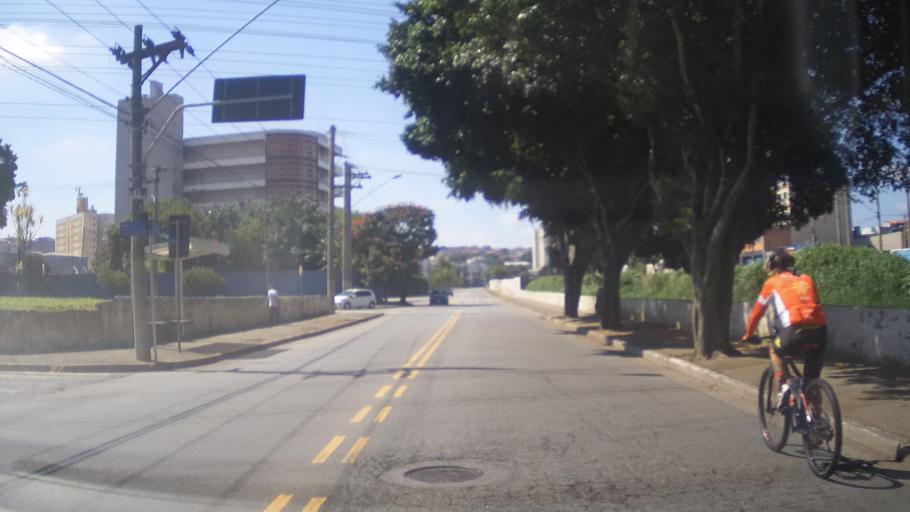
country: BR
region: Sao Paulo
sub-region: Sao Caetano Do Sul
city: Sao Caetano do Sul
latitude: -23.6498
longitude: -46.5682
